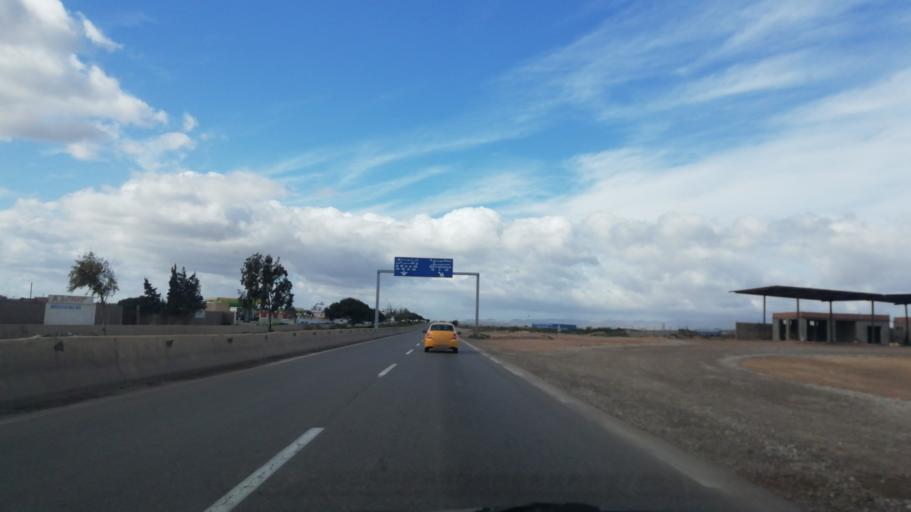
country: DZ
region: Oran
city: Ain el Bya
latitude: 35.7797
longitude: -0.2706
